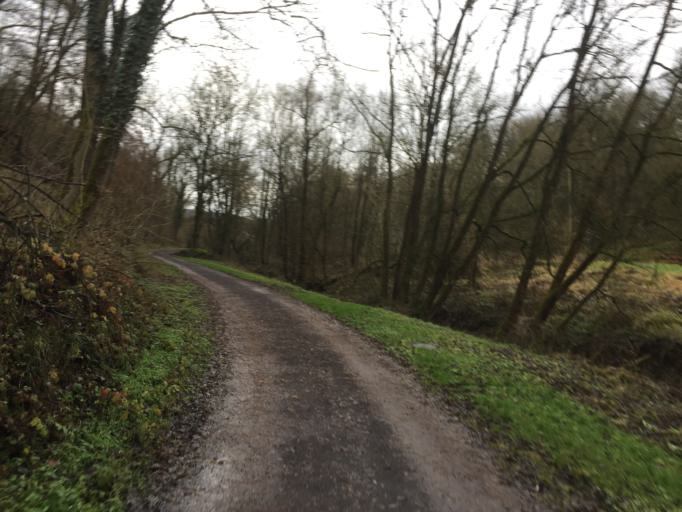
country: DE
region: Hesse
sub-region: Regierungsbezirk Giessen
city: Grunberg
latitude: 50.5904
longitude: 8.9639
